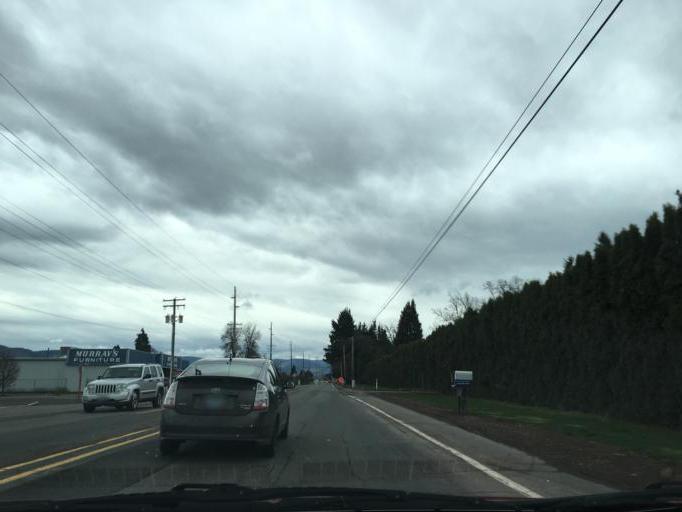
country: US
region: Oregon
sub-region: Hood River County
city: Hood River
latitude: 45.6926
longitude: -121.5237
